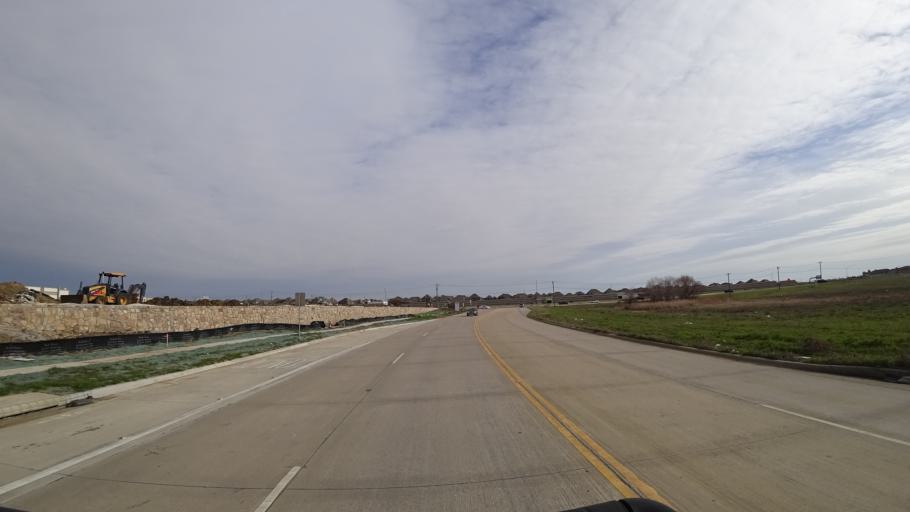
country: US
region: Texas
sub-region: Denton County
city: The Colony
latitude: 33.0589
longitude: -96.9091
